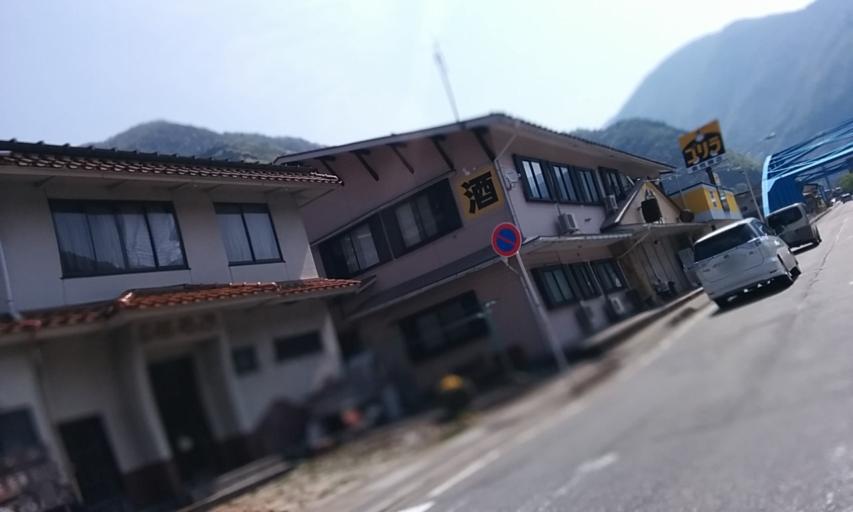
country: JP
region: Gifu
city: Takayama
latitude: 36.2481
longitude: 137.5158
